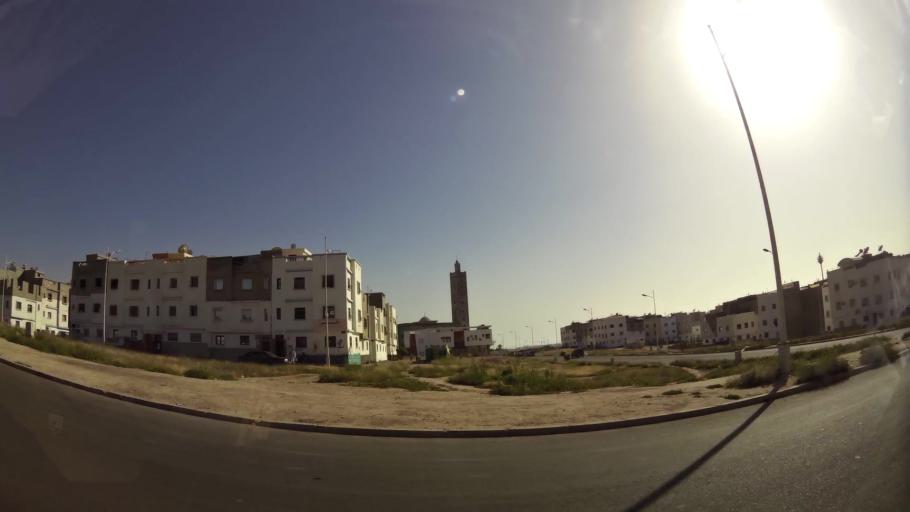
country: MA
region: Oued ed Dahab-Lagouira
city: Dakhla
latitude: 30.4251
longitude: -9.5742
